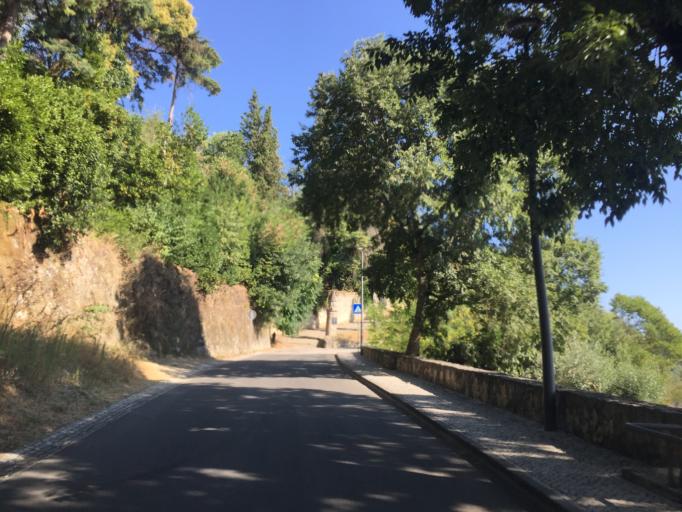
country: PT
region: Santarem
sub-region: Tomar
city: Tomar
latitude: 39.6027
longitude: -8.4158
